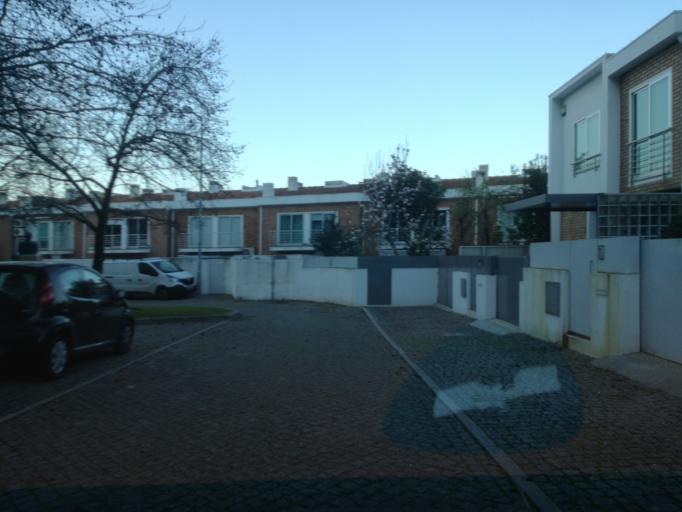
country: PT
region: Porto
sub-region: Maia
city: Leca do Bailio
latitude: 41.2235
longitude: -8.6059
